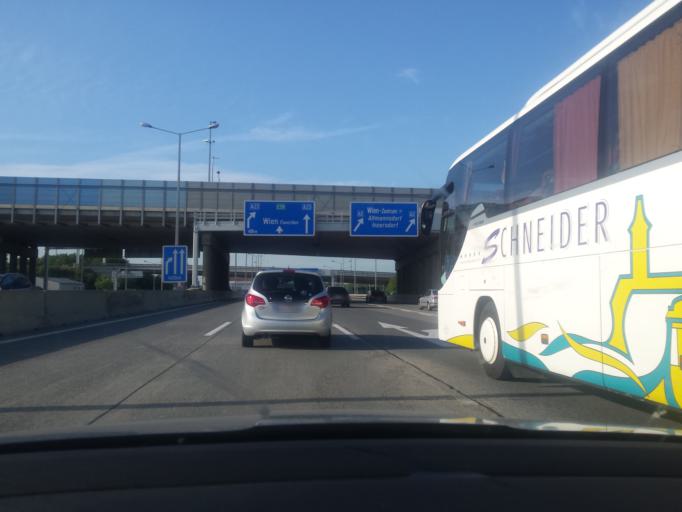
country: AT
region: Lower Austria
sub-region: Politischer Bezirk Modling
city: Vosendorf
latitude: 48.1185
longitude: 16.3239
